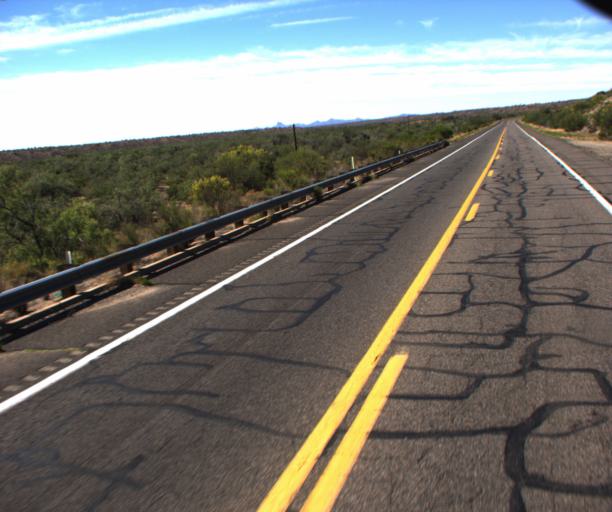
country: US
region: Arizona
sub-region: Yavapai County
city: Congress
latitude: 34.1737
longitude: -112.8329
